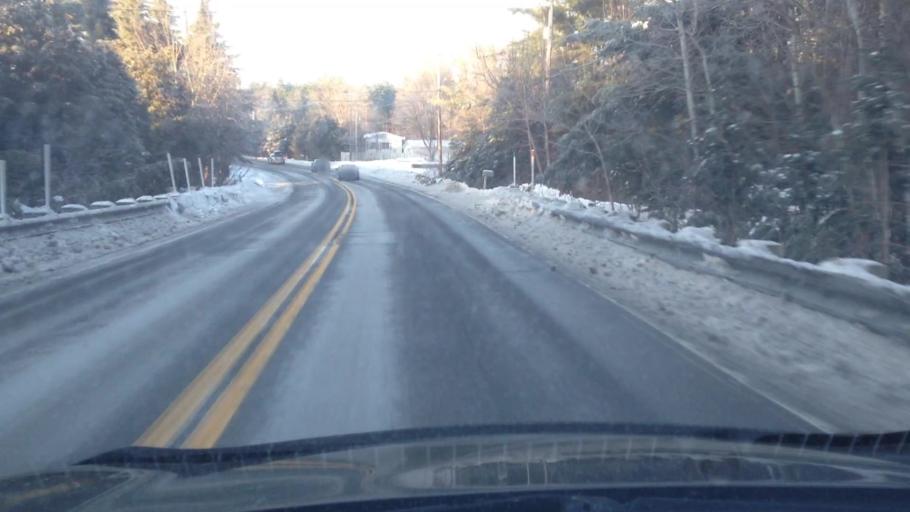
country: CA
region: Quebec
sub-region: Lanaudiere
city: Sainte-Julienne
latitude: 45.9242
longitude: -73.7392
